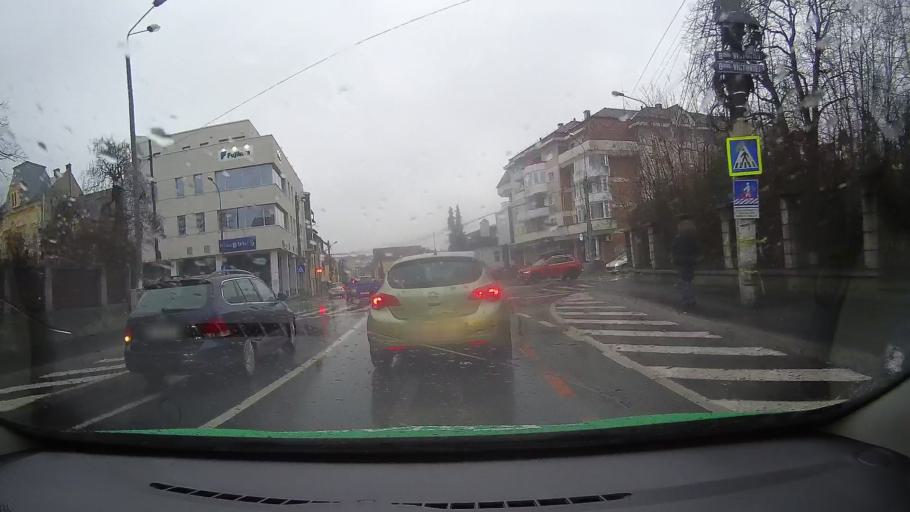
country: RO
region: Sibiu
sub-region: Municipiul Sibiu
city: Sibiu
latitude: 45.7885
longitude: 24.1421
